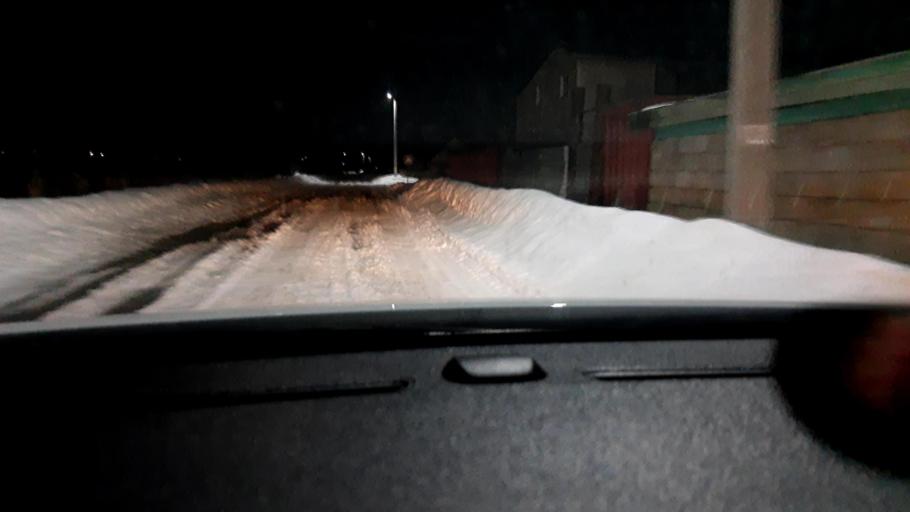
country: RU
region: Bashkortostan
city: Avdon
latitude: 54.5026
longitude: 55.8534
